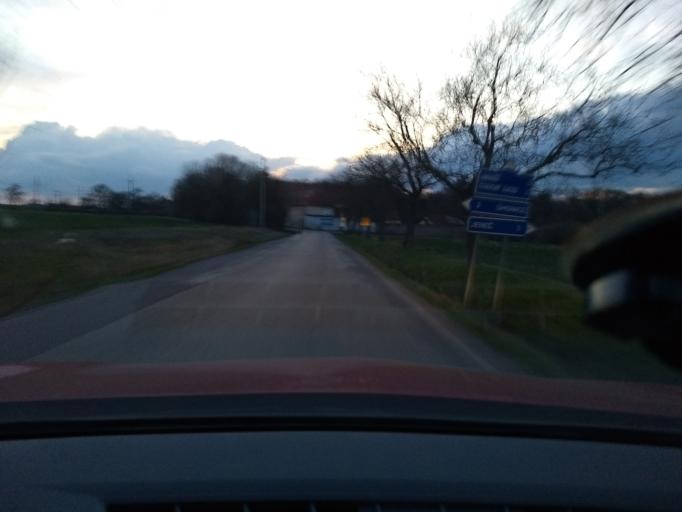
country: CZ
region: Central Bohemia
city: Jenec
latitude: 50.0677
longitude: 14.1900
